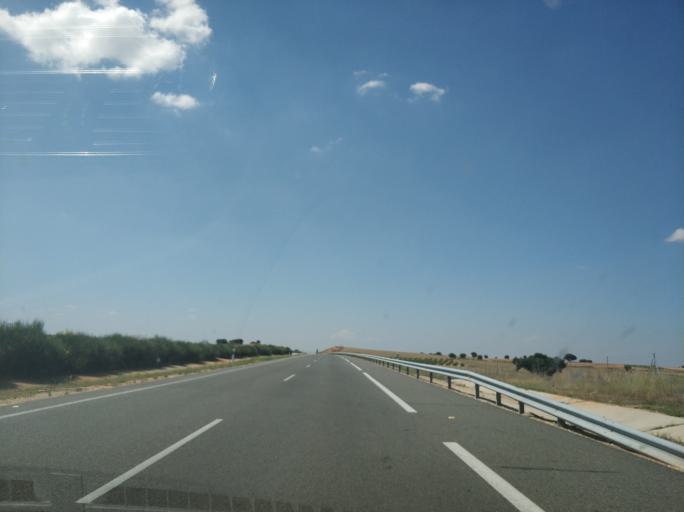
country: ES
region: Castille and Leon
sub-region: Provincia de Zamora
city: Cuelgamures
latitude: 41.2991
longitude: -5.7034
